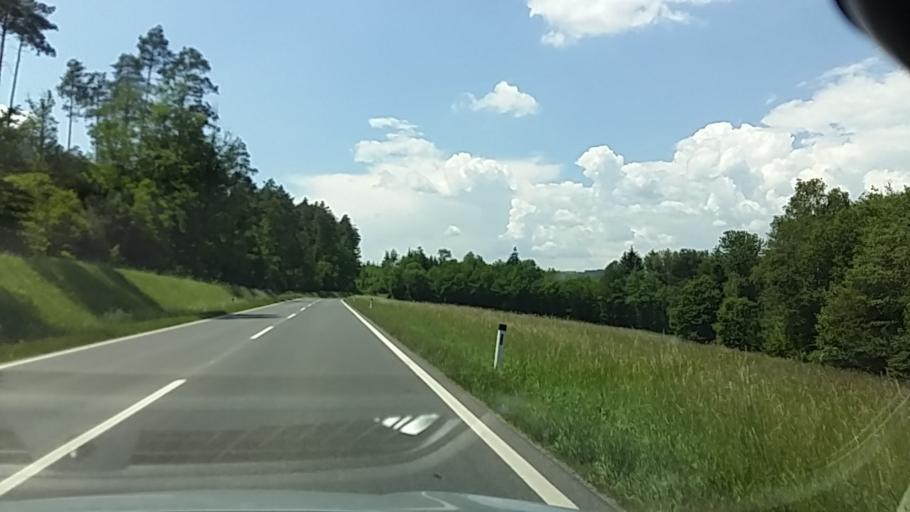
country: AT
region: Burgenland
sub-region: Politischer Bezirk Oberwart
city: Unterkohlstatten
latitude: 47.3951
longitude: 16.3578
